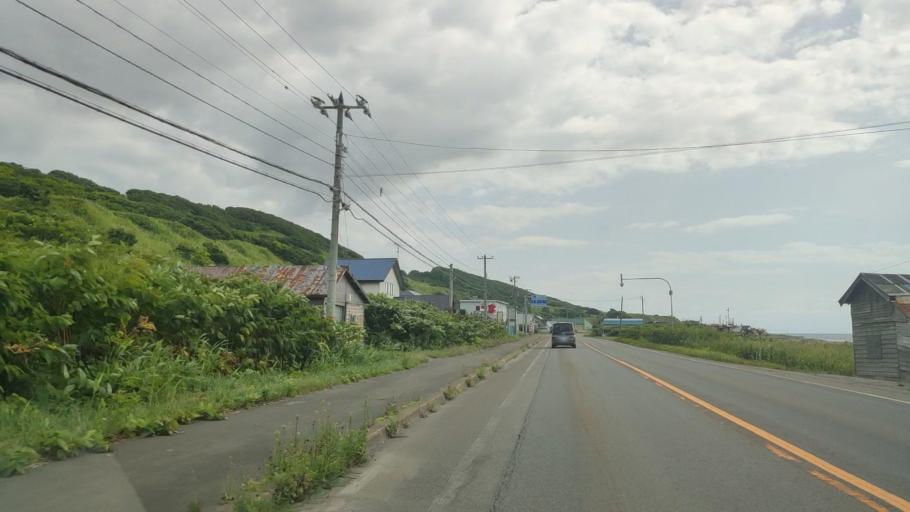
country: JP
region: Hokkaido
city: Rumoi
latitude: 44.1460
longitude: 141.6546
